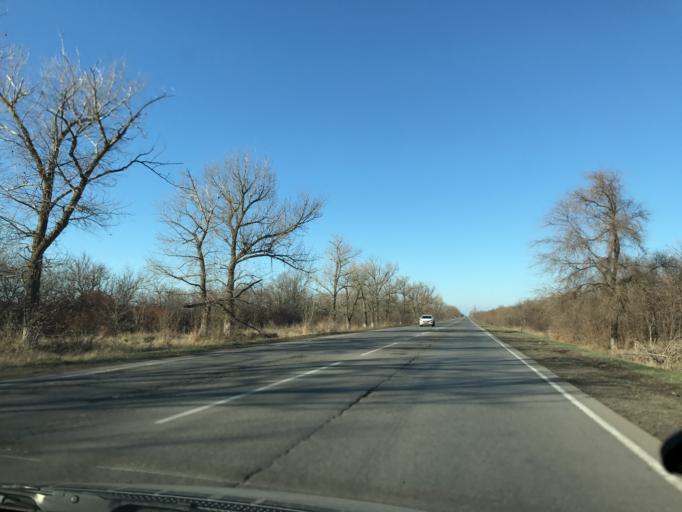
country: RU
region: Rostov
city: Kirovskaya
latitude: 47.0186
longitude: 39.9036
